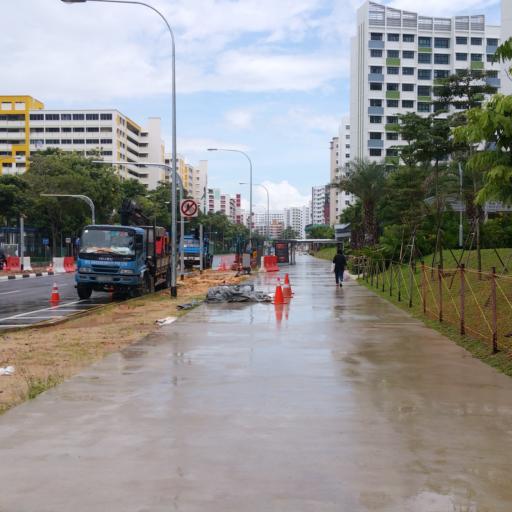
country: MY
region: Johor
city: Kampung Pasir Gudang Baru
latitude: 1.4148
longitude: 103.8394
